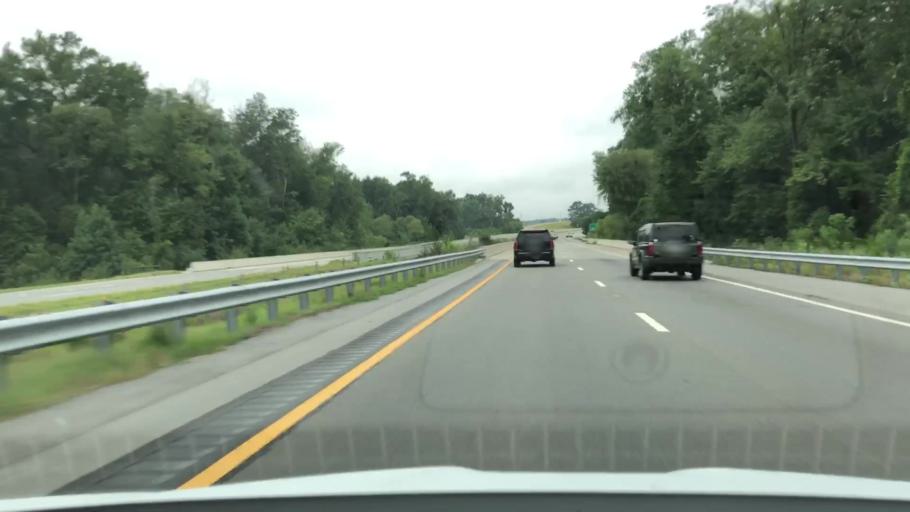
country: US
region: North Carolina
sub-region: Wayne County
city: Goldsboro
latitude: 35.4180
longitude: -77.9262
